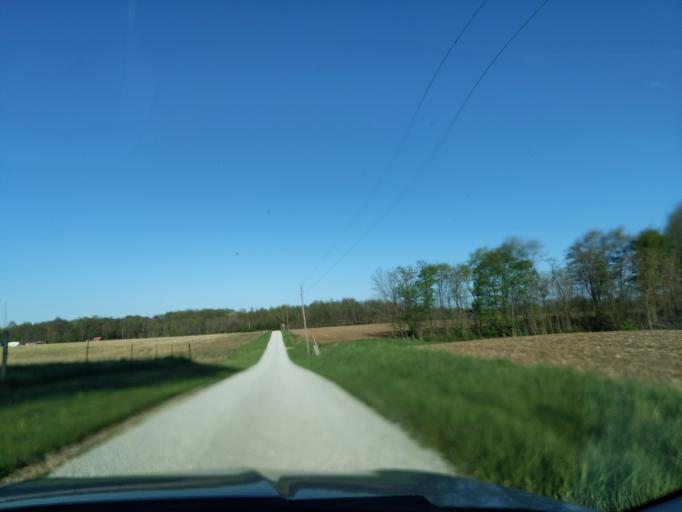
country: US
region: Indiana
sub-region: Decatur County
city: Westport
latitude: 39.1970
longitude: -85.4498
